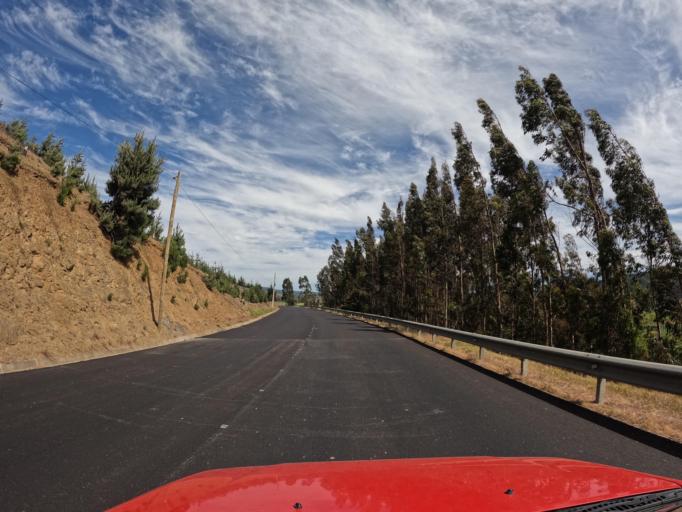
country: CL
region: Maule
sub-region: Provincia de Talca
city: Constitucion
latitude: -35.0523
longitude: -72.0456
